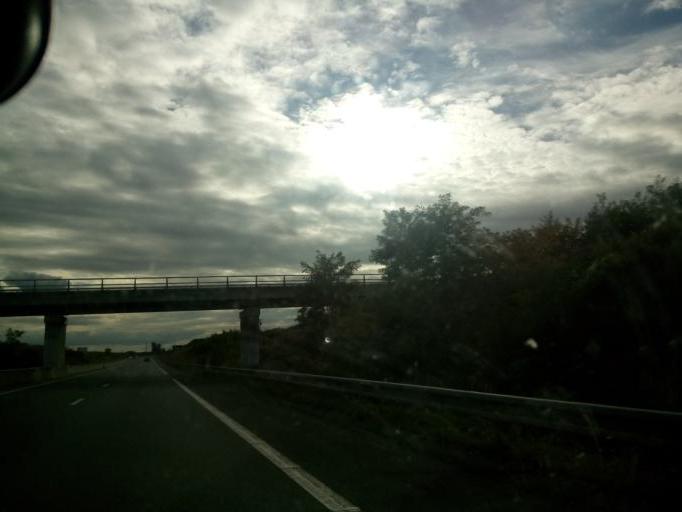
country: FR
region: Centre
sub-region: Departement d'Indre-et-Loire
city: Montbazon
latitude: 47.3070
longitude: 0.7117
